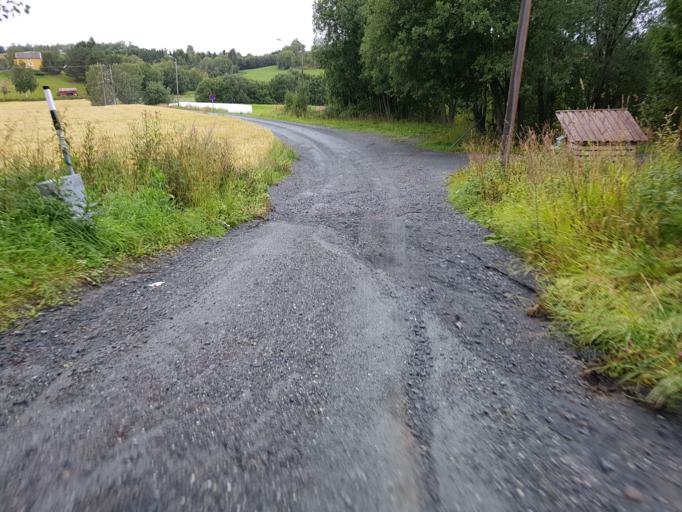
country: NO
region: Sor-Trondelag
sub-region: Trondheim
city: Trondheim
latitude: 63.3997
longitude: 10.4652
